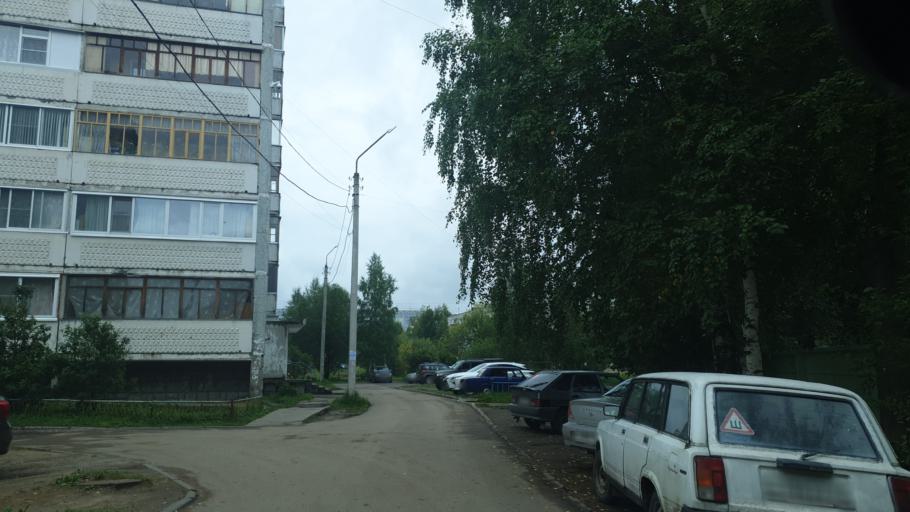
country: RU
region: Komi Republic
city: Ezhva
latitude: 61.7835
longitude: 50.7555
